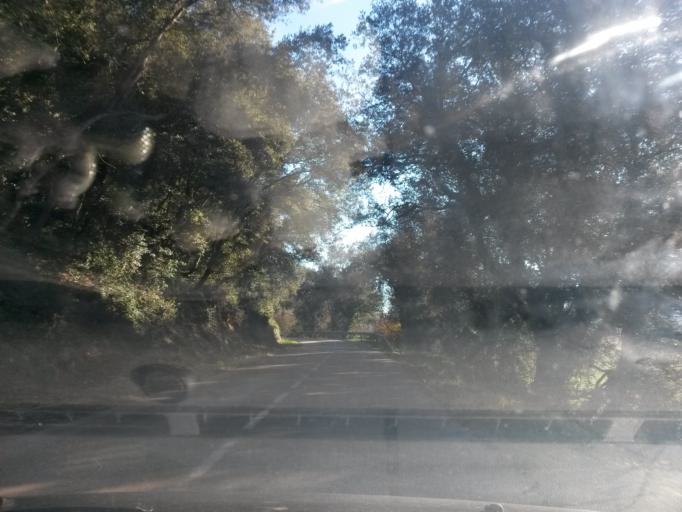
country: ES
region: Catalonia
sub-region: Provincia de Girona
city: Sant Gregori
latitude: 41.9814
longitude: 2.6849
